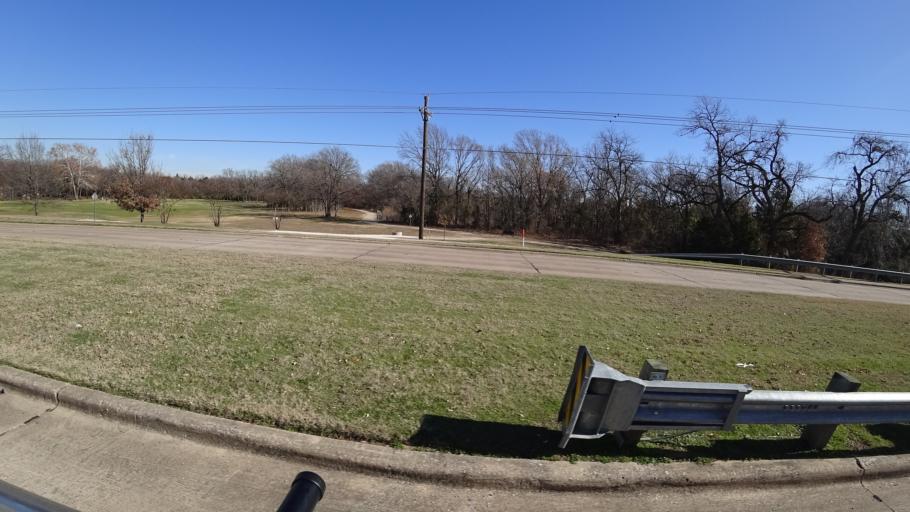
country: US
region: Texas
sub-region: Denton County
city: Lewisville
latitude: 33.0152
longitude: -97.0050
